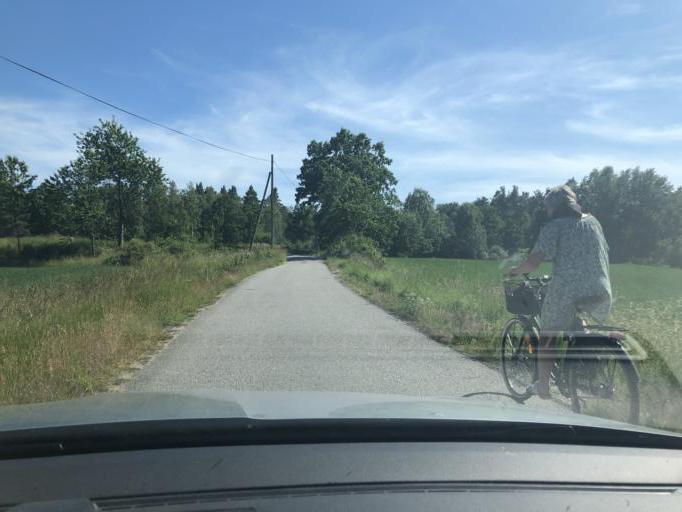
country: SE
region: Blekinge
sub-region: Karlshamns Kommun
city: Morrum
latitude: 56.1570
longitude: 14.8005
